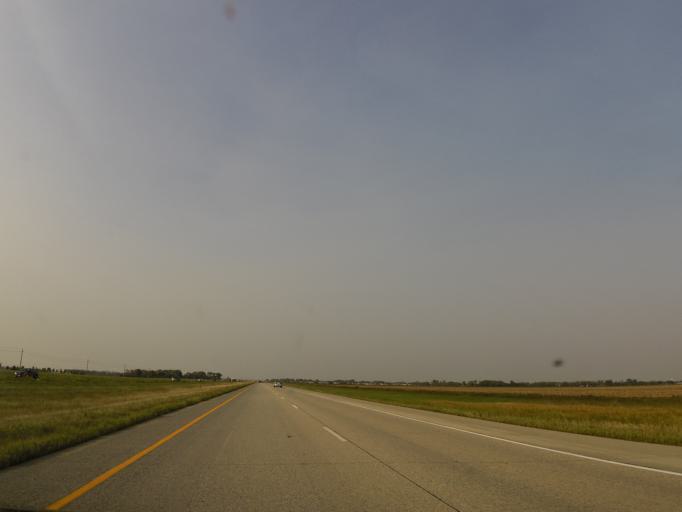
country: US
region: North Dakota
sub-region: Cass County
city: Horace
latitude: 46.7754
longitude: -96.8391
